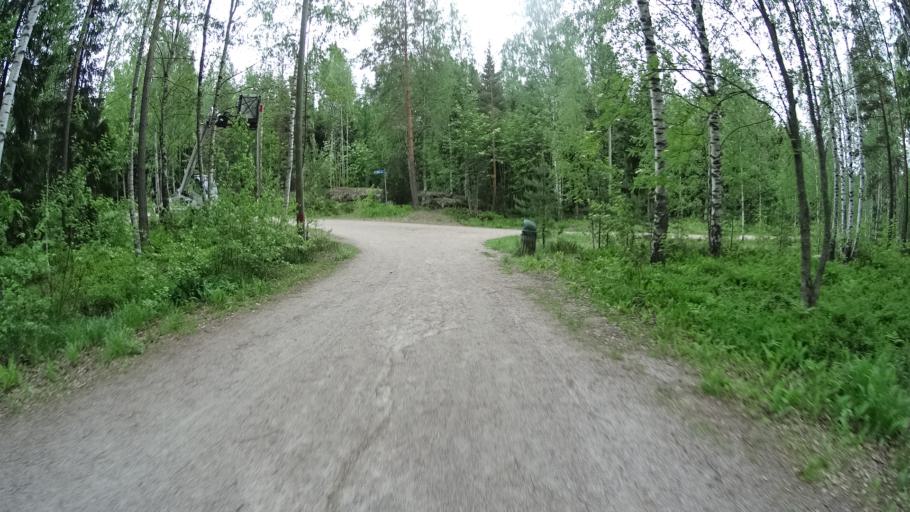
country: FI
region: Uusimaa
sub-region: Helsinki
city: Vantaa
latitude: 60.2502
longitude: 25.0721
